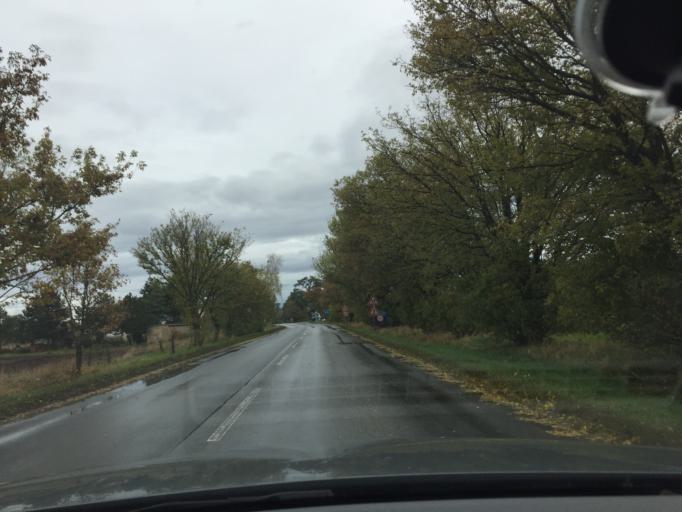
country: CZ
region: Central Bohemia
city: Velvary
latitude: 50.3338
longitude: 14.2851
